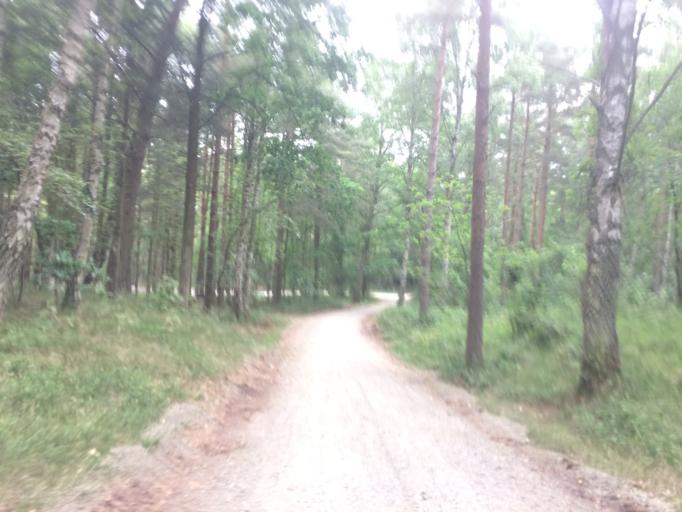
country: DK
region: Capital Region
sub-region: Bornholm Kommune
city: Ronne
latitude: 55.1268
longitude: 14.7120
